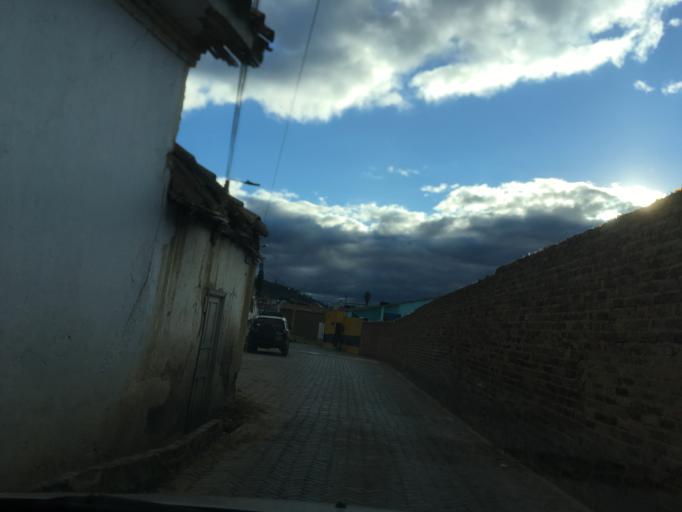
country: CO
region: Boyaca
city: Sogamoso
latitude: 5.7164
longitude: -72.9233
